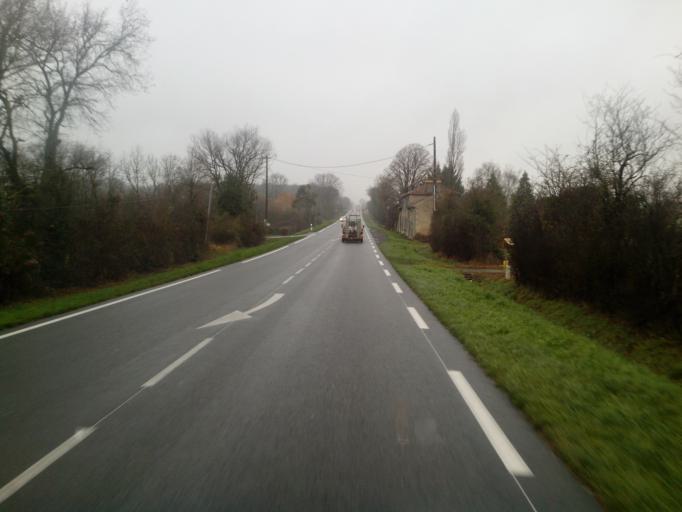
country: FR
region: Poitou-Charentes
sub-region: Departement de la Vienne
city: Savigny-Levescault
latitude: 46.5239
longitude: 0.4466
